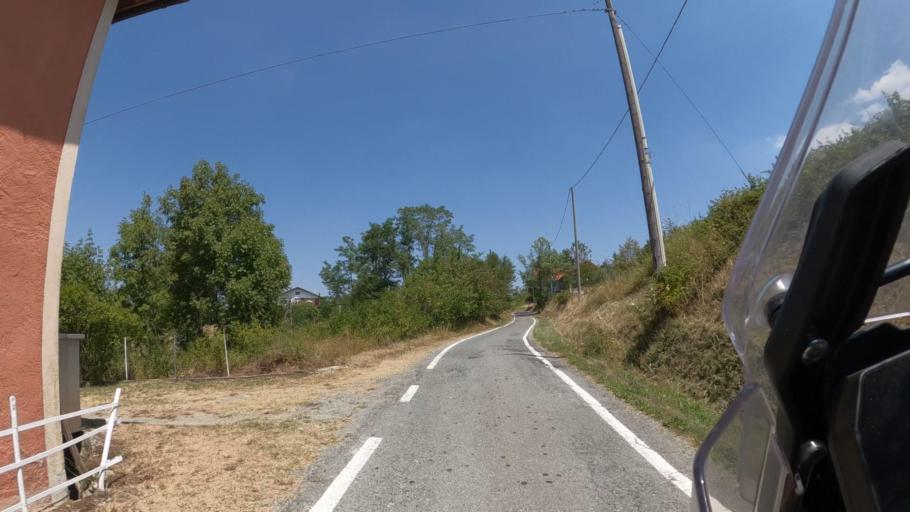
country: IT
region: Piedmont
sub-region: Provincia di Alessandria
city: Ponzone
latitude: 44.5468
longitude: 8.4812
